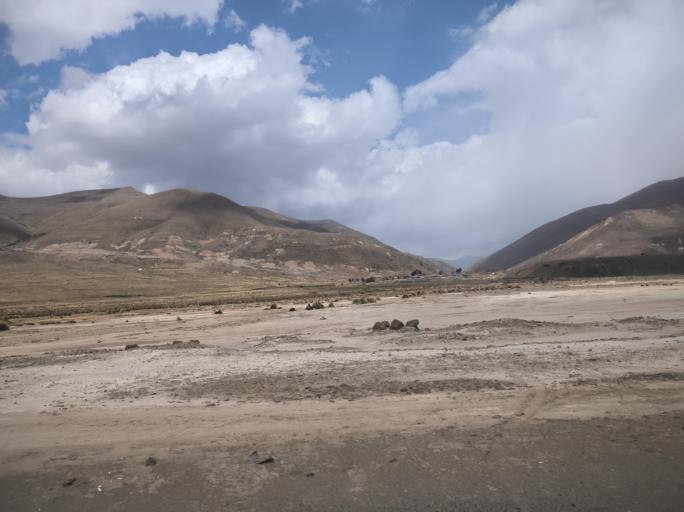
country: BO
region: Oruro
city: Poopo
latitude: -18.3774
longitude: -66.9797
